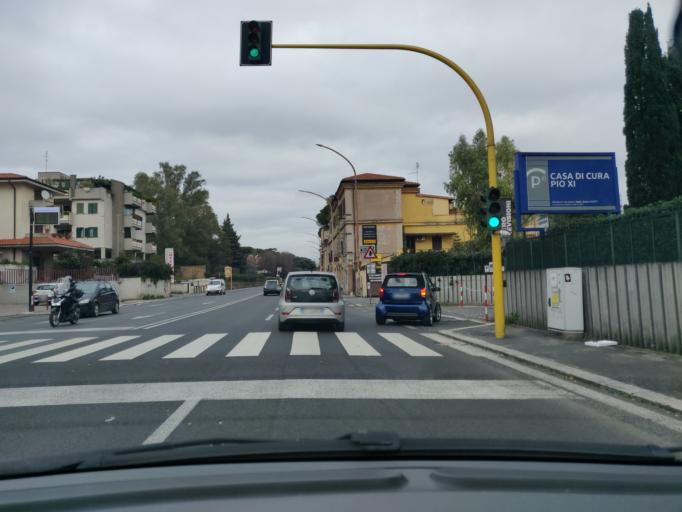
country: VA
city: Vatican City
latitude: 41.8963
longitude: 12.4196
